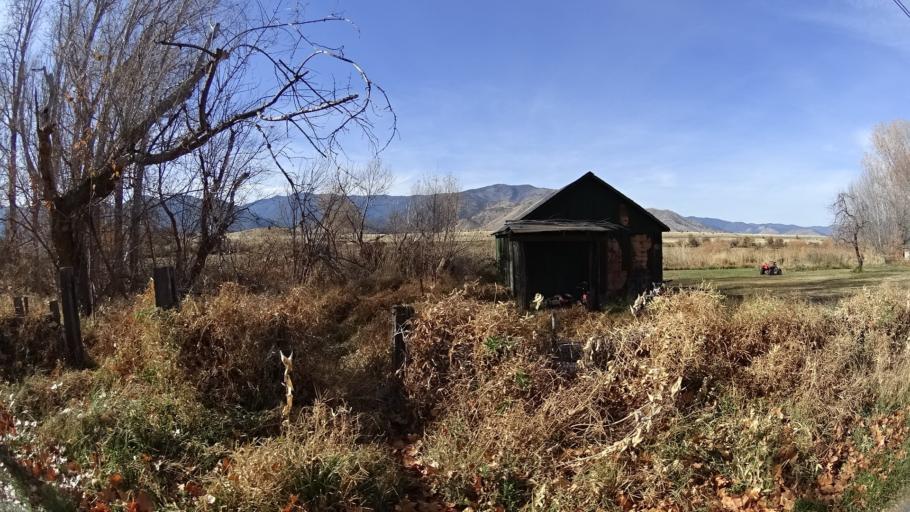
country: US
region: California
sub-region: Siskiyou County
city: Weed
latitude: 41.4607
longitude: -122.4334
